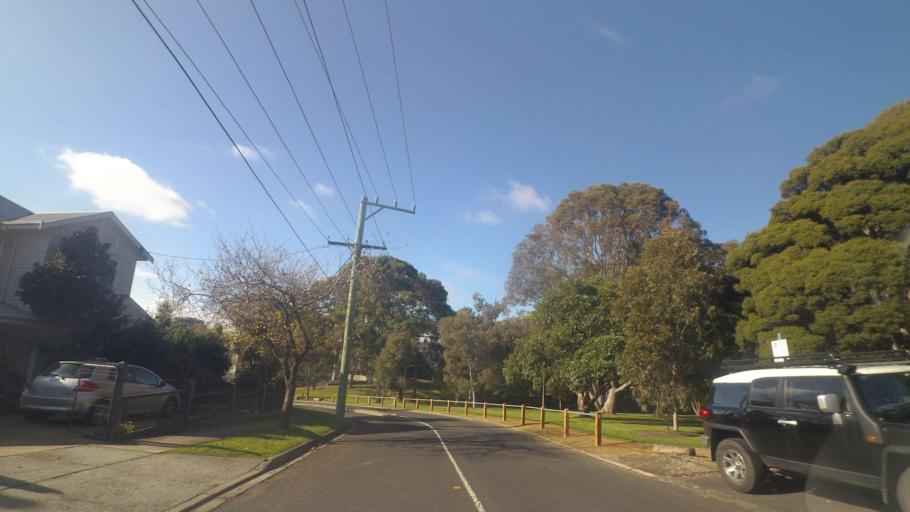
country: AU
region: Victoria
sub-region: Whitehorse
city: Box Hill
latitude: -37.8150
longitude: 145.1131
